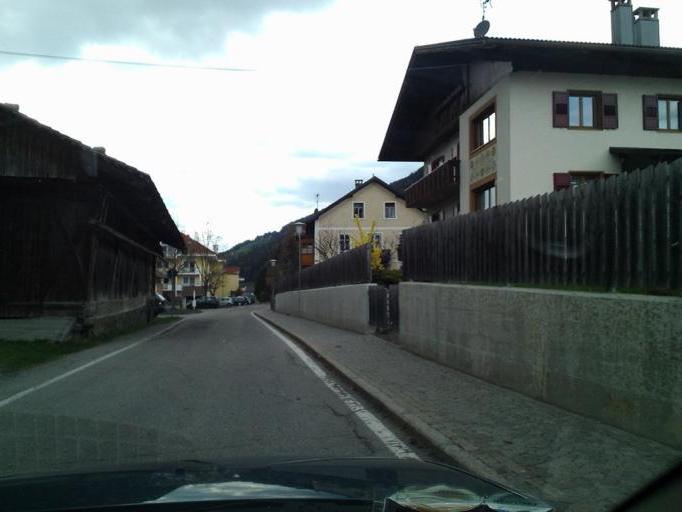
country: IT
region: Trentino-Alto Adige
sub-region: Bolzano
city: Villabassa
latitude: 46.7397
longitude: 12.1690
